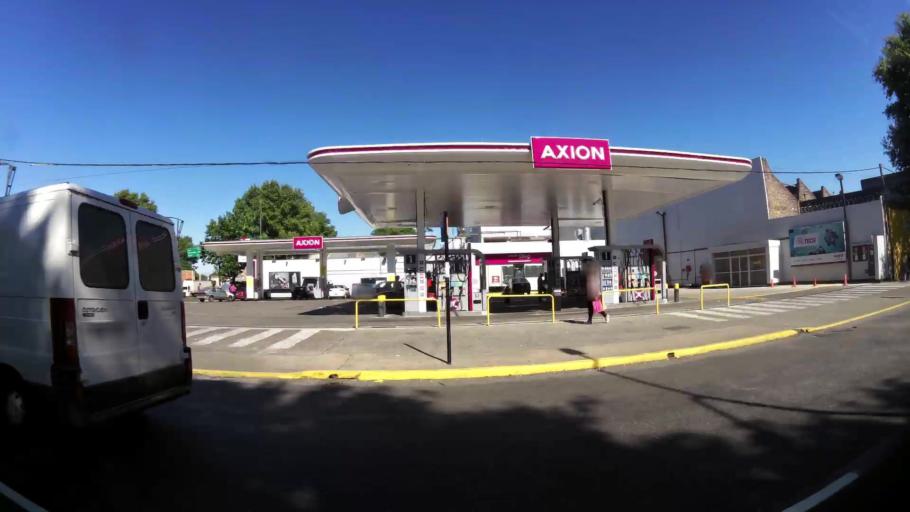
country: AR
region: Santa Fe
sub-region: Departamento de Rosario
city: Rosario
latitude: -32.9496
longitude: -60.6818
